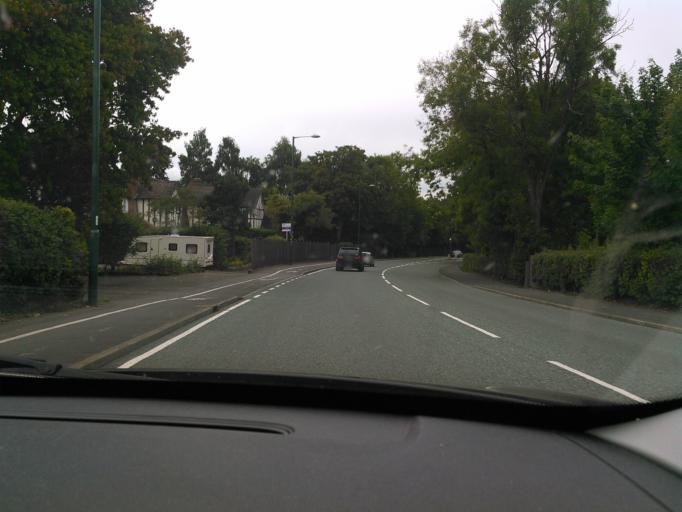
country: GB
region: England
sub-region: Shropshire
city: Shrewsbury
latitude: 52.6993
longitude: -2.7691
